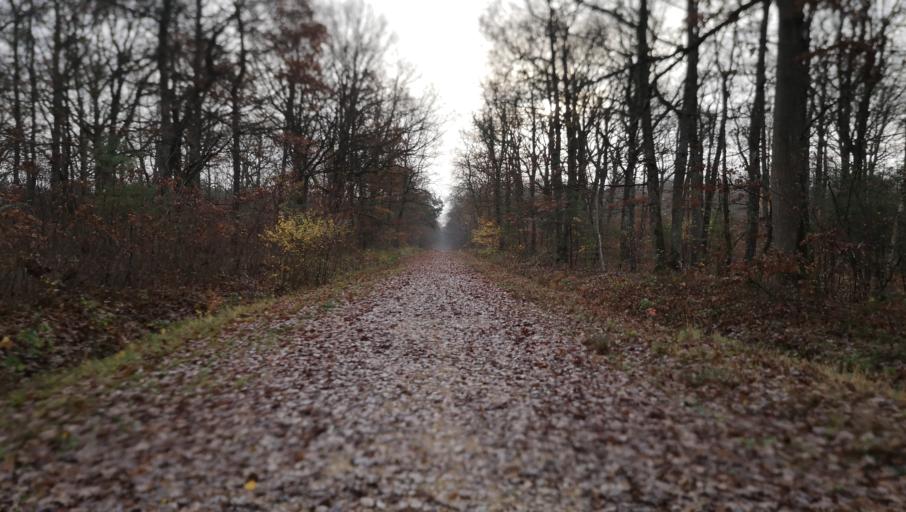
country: FR
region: Centre
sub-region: Departement du Loiret
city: Chanteau
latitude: 47.9457
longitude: 1.9681
